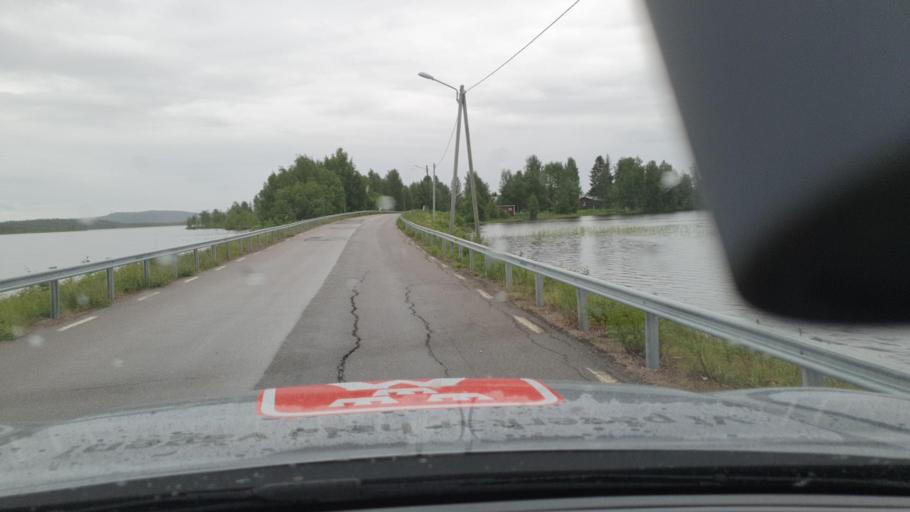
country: SE
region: Norrbotten
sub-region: Pajala Kommun
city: Pajala
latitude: 66.8012
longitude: 23.1223
